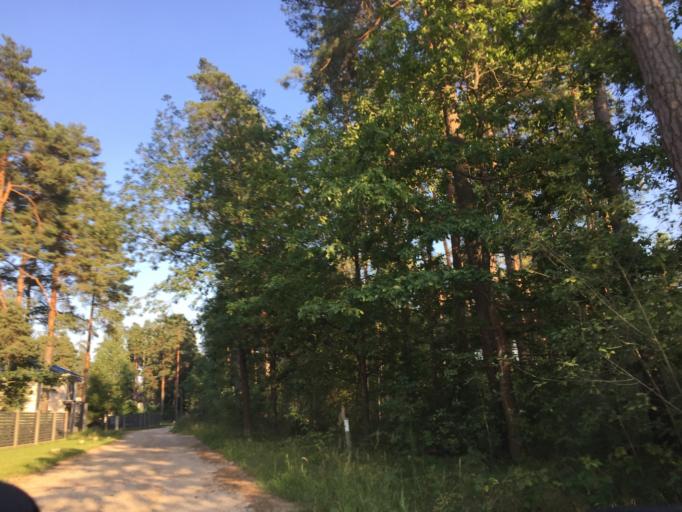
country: LV
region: Riga
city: Bergi
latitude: 56.9772
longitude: 24.3691
